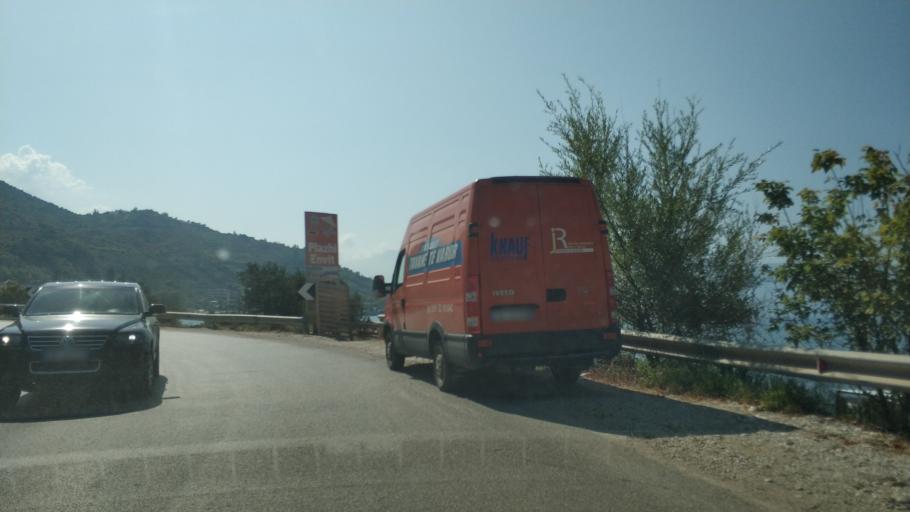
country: AL
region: Vlore
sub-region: Rrethi i Vlores
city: Orikum
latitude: 40.3886
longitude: 19.4819
